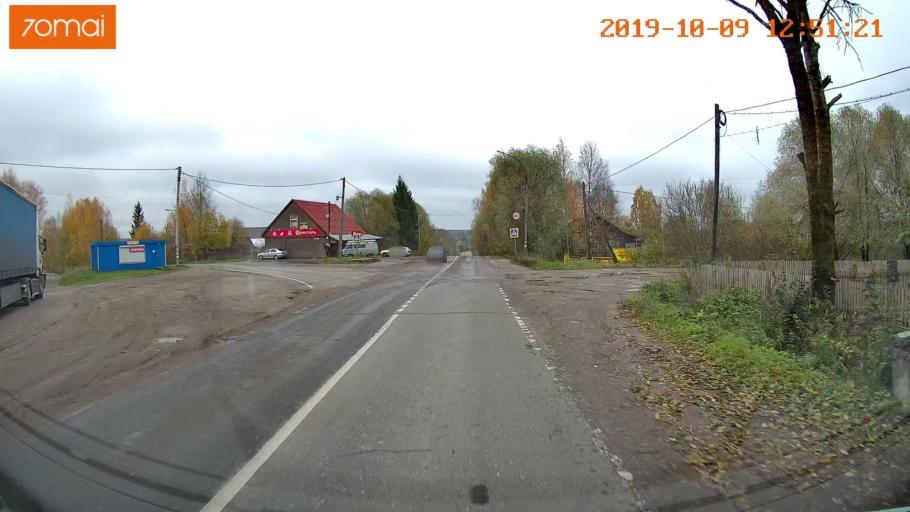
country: RU
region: Jaroslavl
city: Prechistoye
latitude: 58.4200
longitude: 40.3406
